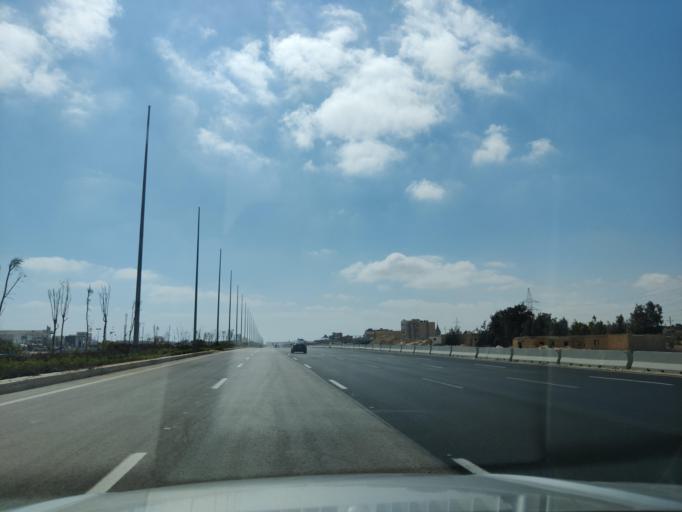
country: EG
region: Muhafazat Matruh
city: Al `Alamayn
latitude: 30.9921
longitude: 28.6740
